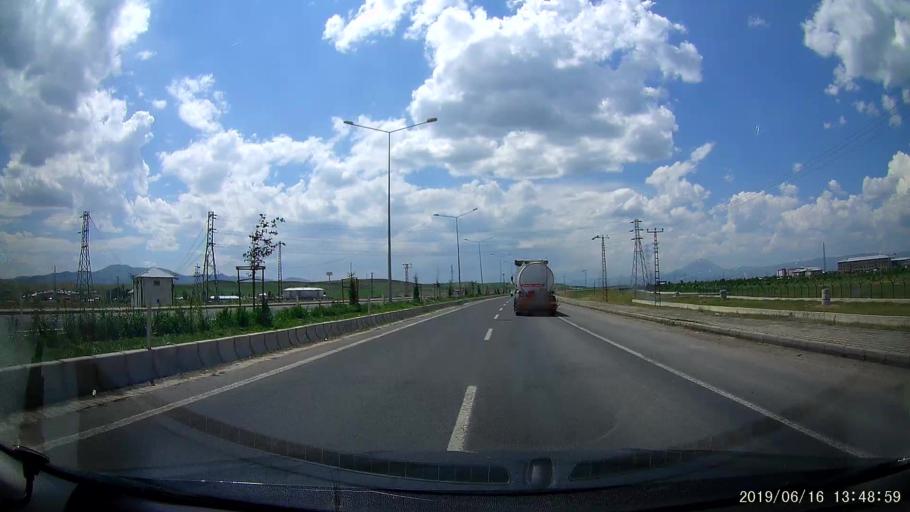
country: TR
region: Agri
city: Agri
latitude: 39.7148
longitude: 42.9979
